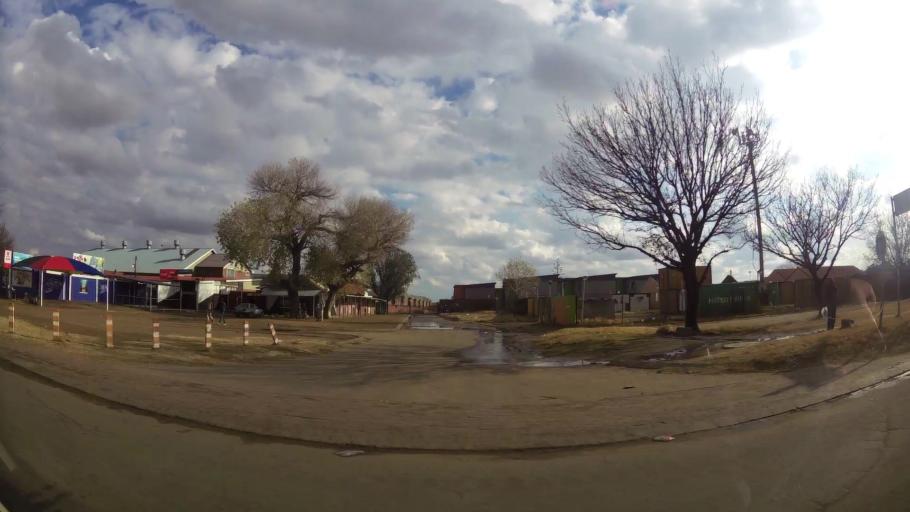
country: ZA
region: Orange Free State
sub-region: Fezile Dabi District Municipality
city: Sasolburg
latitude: -26.8361
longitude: 27.8427
